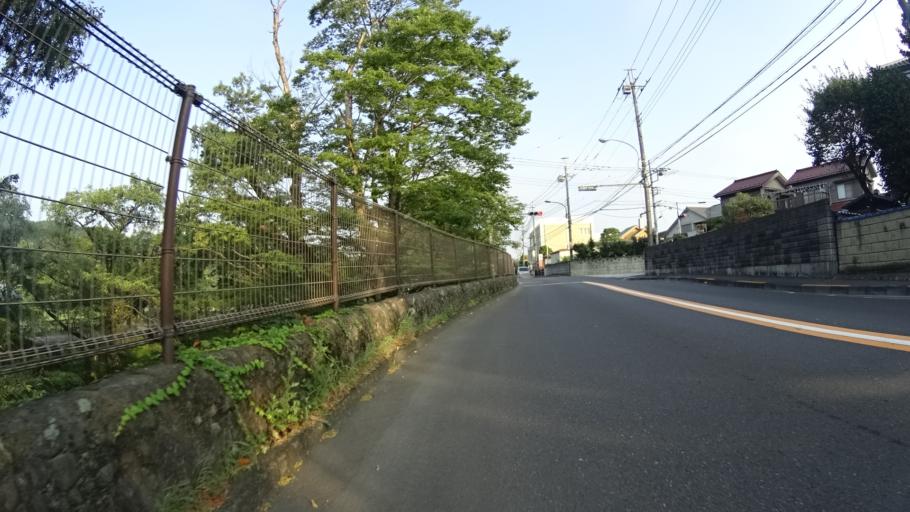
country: JP
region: Tokyo
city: Fussa
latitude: 35.7553
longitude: 139.3097
